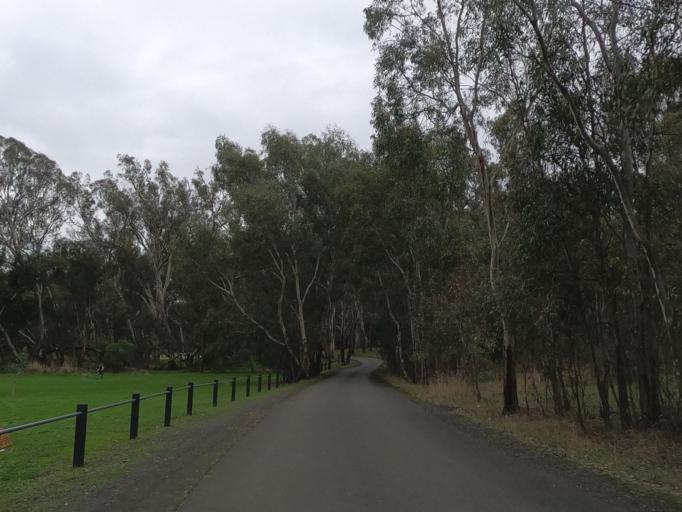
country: AU
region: Victoria
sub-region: Greater Bendigo
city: Kangaroo Flat
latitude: -36.8414
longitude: 144.1556
